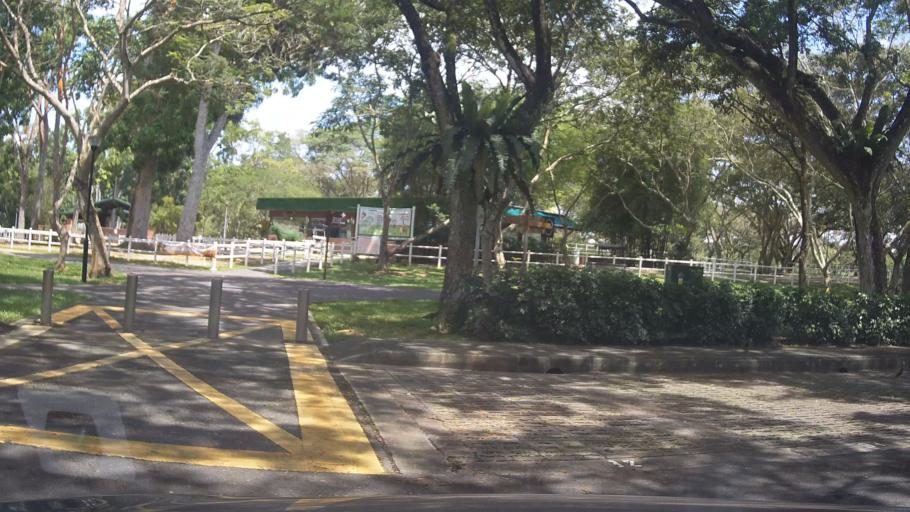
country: MY
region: Johor
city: Kampung Pasir Gudang Baru
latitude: 1.3789
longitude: 103.9479
